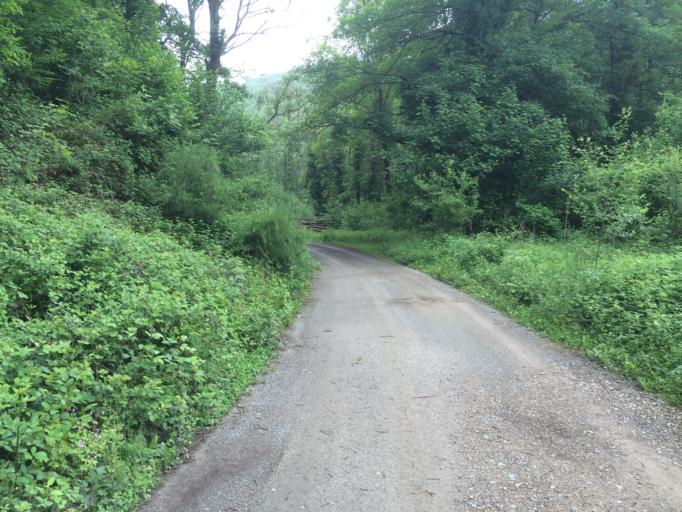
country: BE
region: Wallonia
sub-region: Province de Namur
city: Yvoir
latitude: 50.3210
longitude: 4.9471
